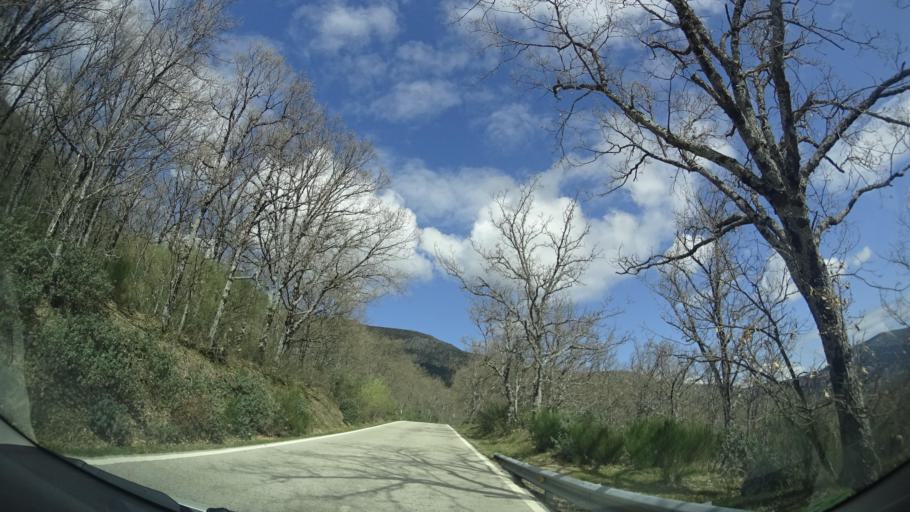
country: ES
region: Madrid
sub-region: Provincia de Madrid
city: Miraflores de la Sierra
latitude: 40.8291
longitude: -3.7660
